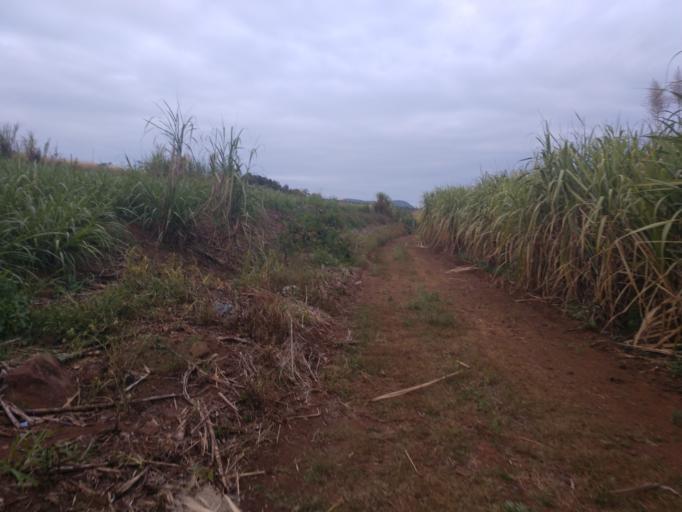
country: MX
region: Nayarit
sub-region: Tepic
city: La Corregidora
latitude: 21.4778
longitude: -104.8101
